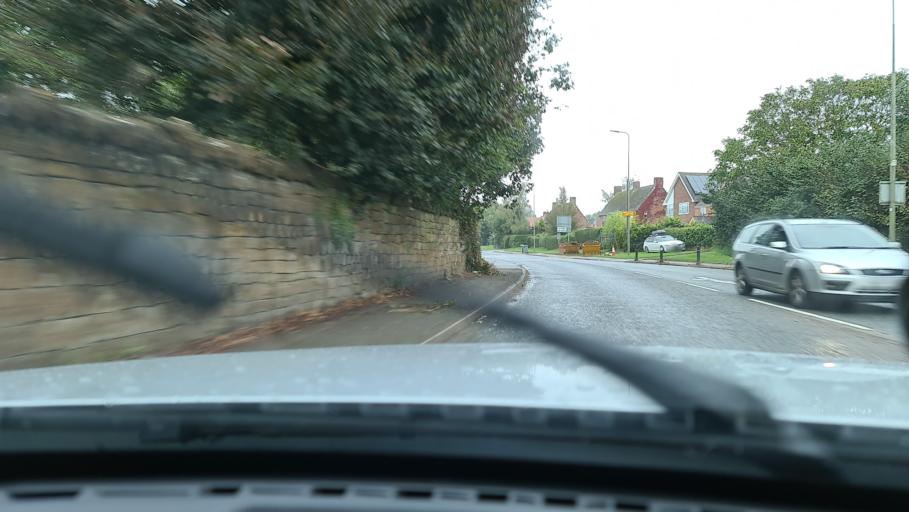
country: GB
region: England
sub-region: Oxfordshire
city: Adderbury
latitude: 52.0190
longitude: -1.3107
